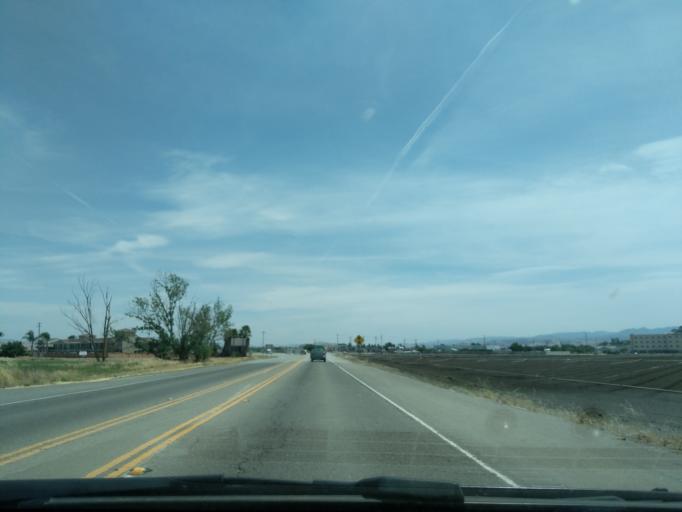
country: US
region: California
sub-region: San Benito County
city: Hollister
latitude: 36.8674
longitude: -121.4045
